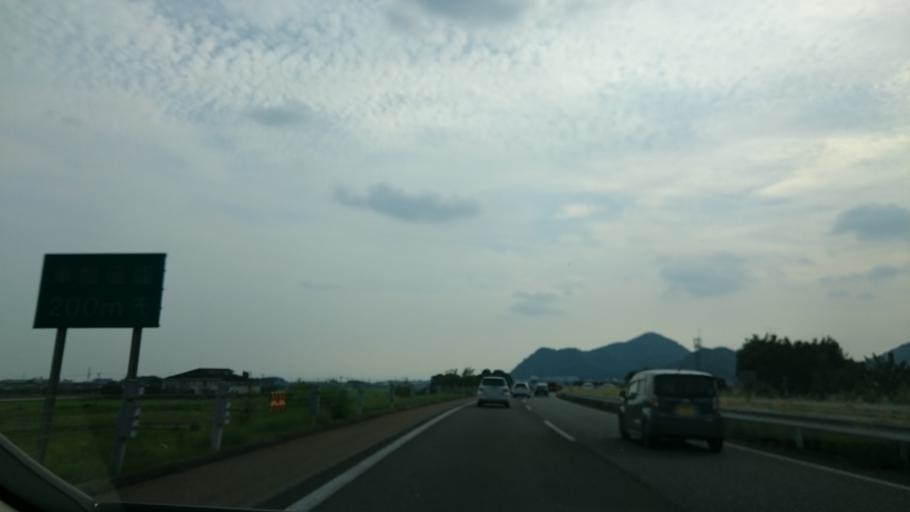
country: JP
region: Gifu
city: Kakamigahara
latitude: 35.4271
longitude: 136.8571
